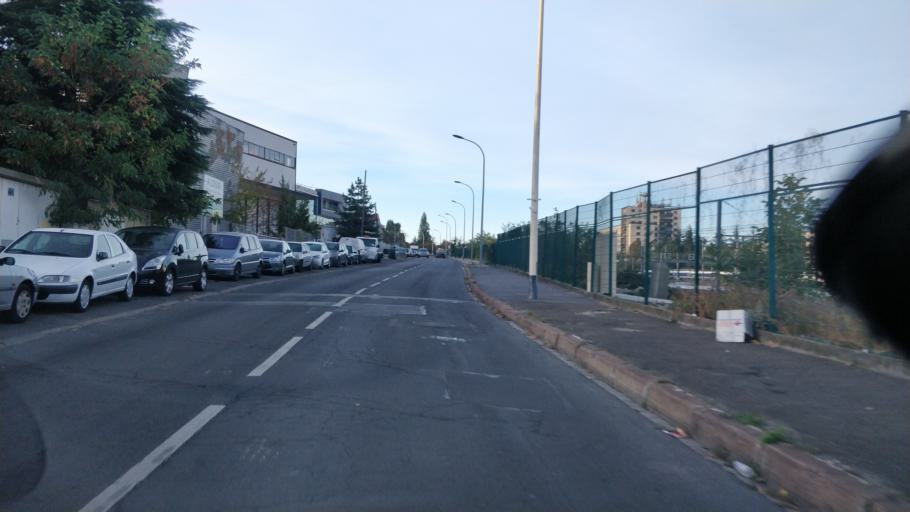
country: FR
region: Ile-de-France
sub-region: Departement des Hauts-de-Seine
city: Chatillon
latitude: 48.8003
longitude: 2.2990
